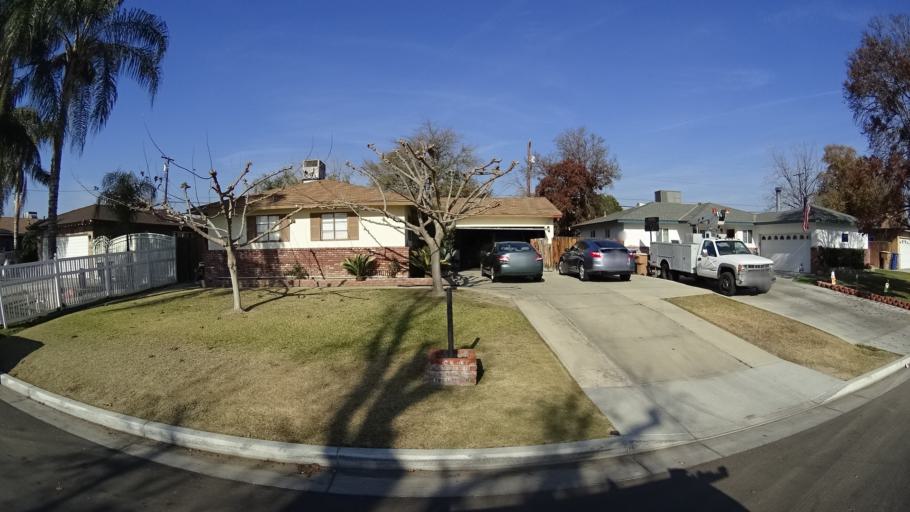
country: US
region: California
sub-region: Kern County
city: Bakersfield
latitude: 35.3282
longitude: -119.0185
